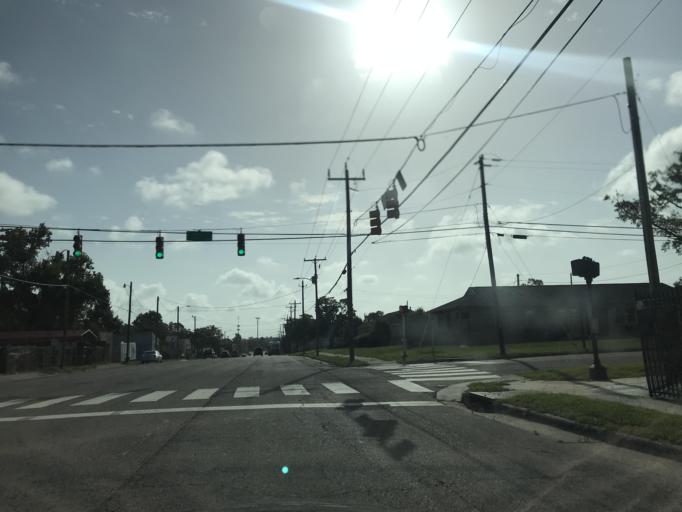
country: US
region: North Carolina
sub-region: New Hanover County
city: Wilmington
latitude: 34.2252
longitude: -77.9318
